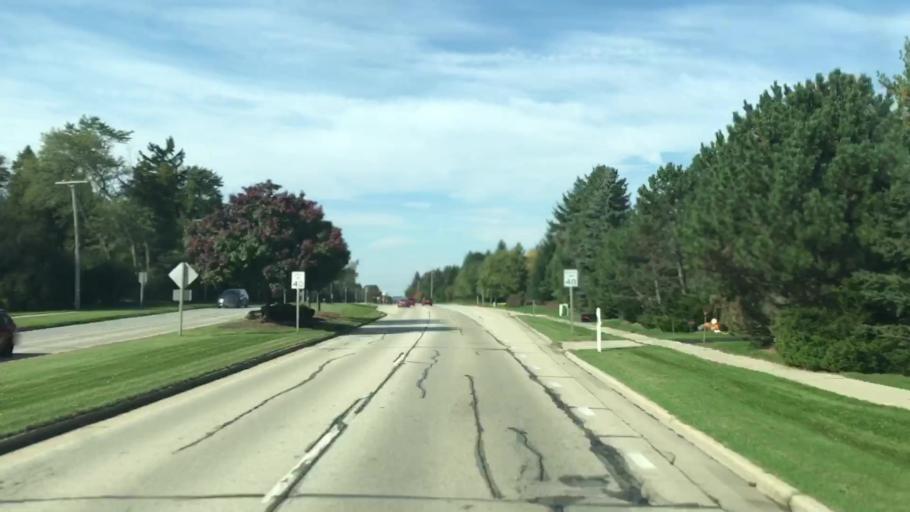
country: US
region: Wisconsin
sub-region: Ozaukee County
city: Thiensville
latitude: 43.2217
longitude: -87.9557
